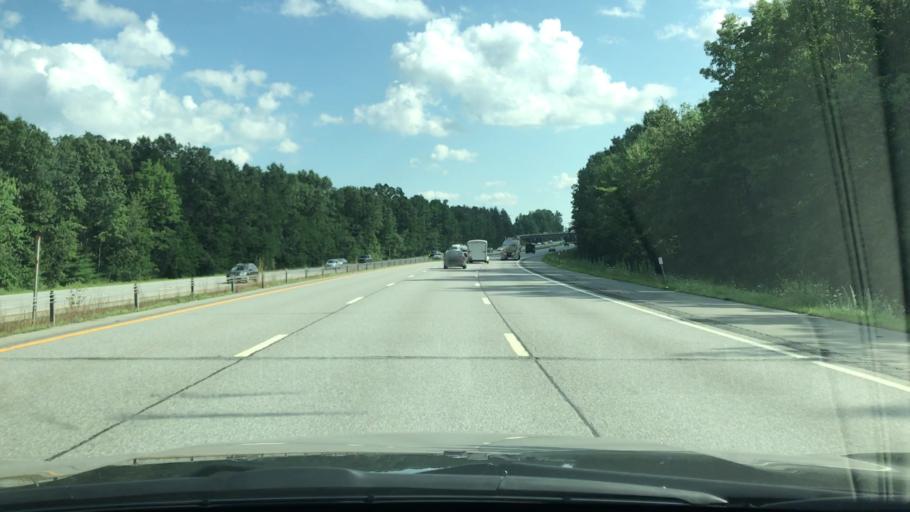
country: US
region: New York
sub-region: Warren County
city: West Glens Falls
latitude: 43.3141
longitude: -73.6750
